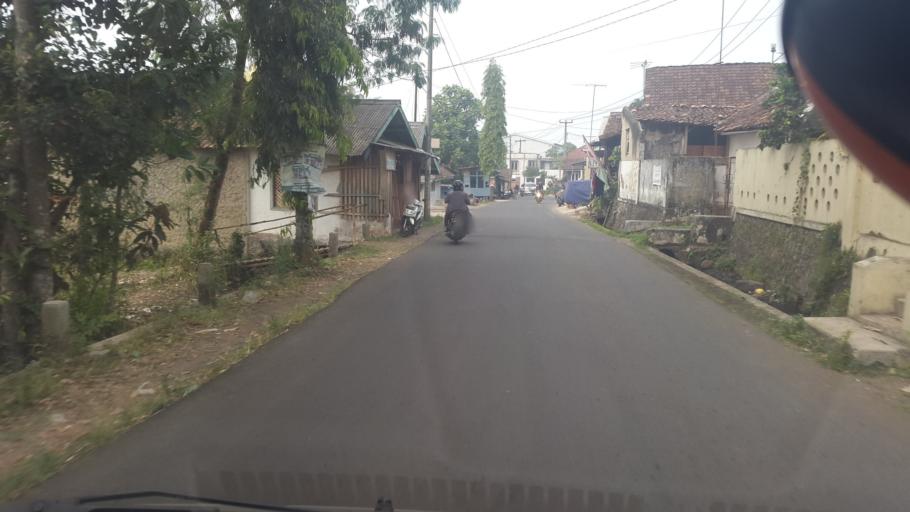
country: ID
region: West Java
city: Sukabumi
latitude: -6.9263
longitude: 106.8994
